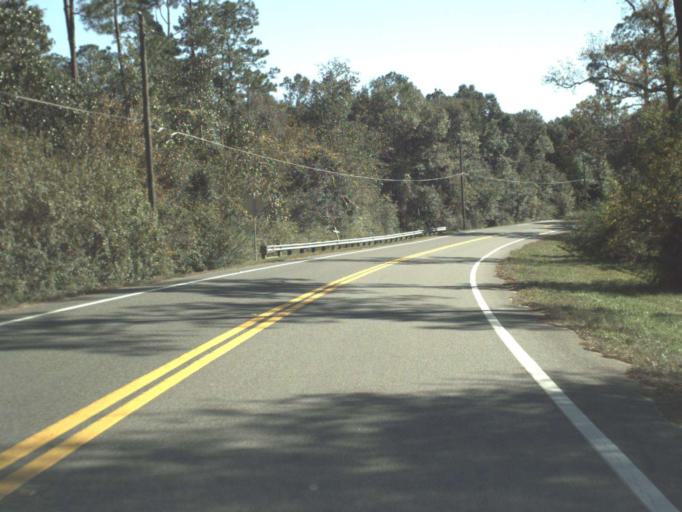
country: US
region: Florida
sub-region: Escambia County
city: Cantonment
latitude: 30.5343
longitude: -87.3988
